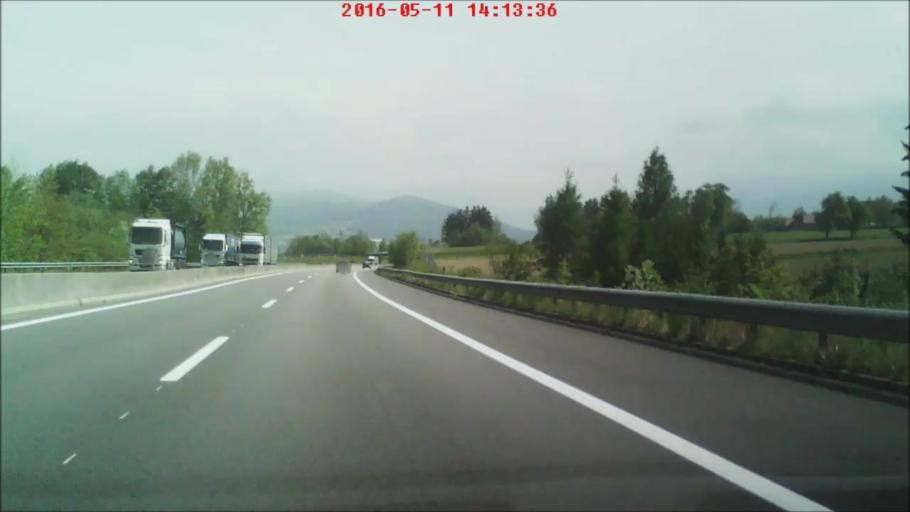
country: AT
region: Upper Austria
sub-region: Politischer Bezirk Kirchdorf an der Krems
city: Kremsmunster
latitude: 47.9941
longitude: 14.0861
